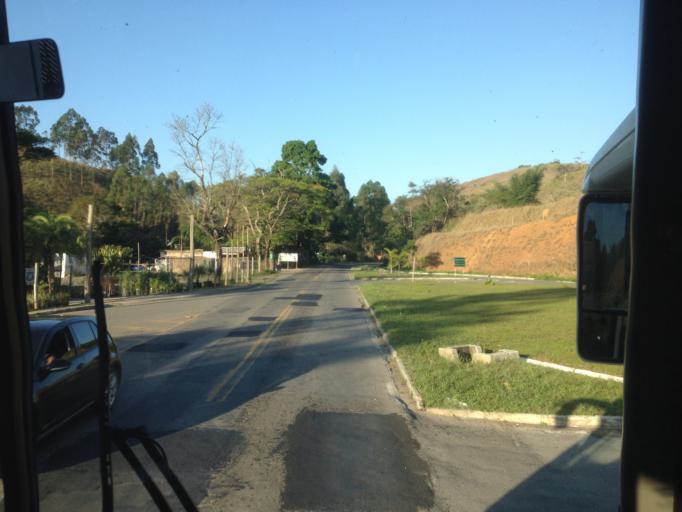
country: BR
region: Minas Gerais
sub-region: Juiz De Fora
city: Juiz de Fora
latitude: -21.6781
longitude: -43.3446
